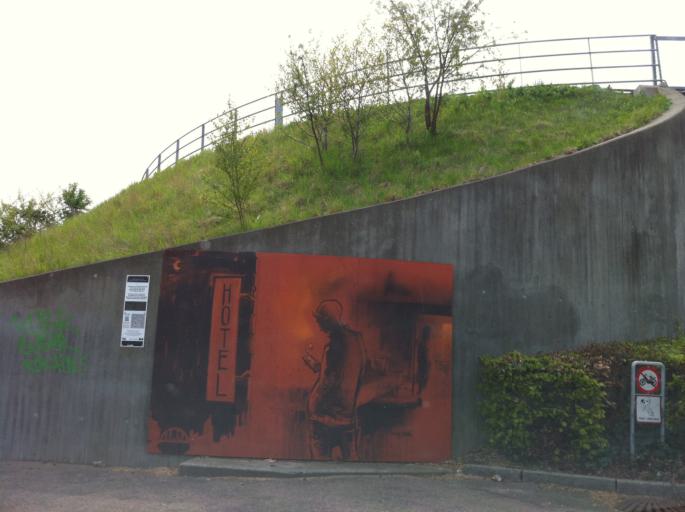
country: DK
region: Zealand
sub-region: Naestved Kommune
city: Naestved
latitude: 55.2329
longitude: 11.7684
